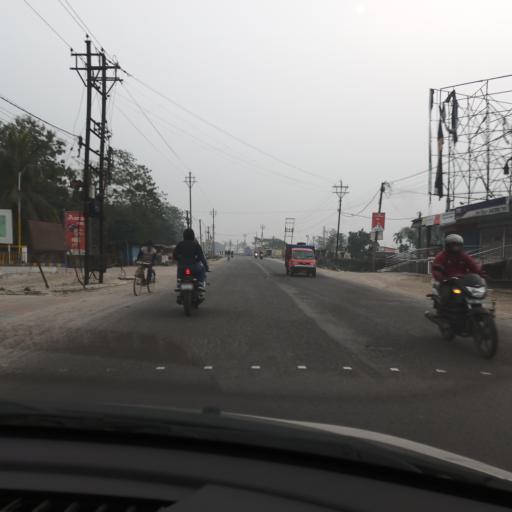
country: IN
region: West Bengal
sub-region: Darjiling
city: Shiliguri
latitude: 26.6768
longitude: 88.4627
